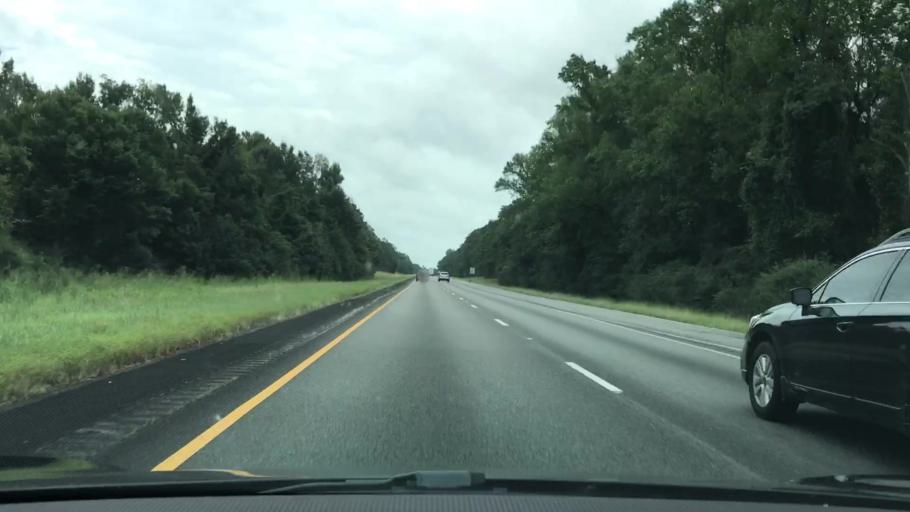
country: US
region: Alabama
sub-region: Elmore County
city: Tallassee
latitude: 32.4322
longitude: -85.8864
